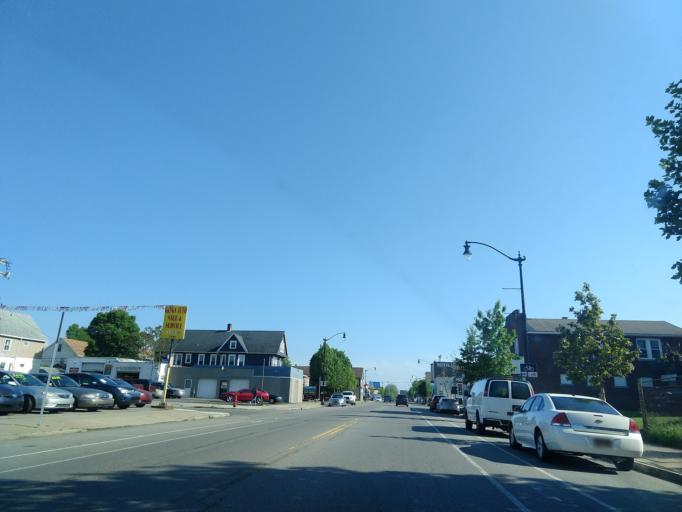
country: US
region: New York
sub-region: Erie County
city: Lackawanna
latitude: 42.8416
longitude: -78.8238
